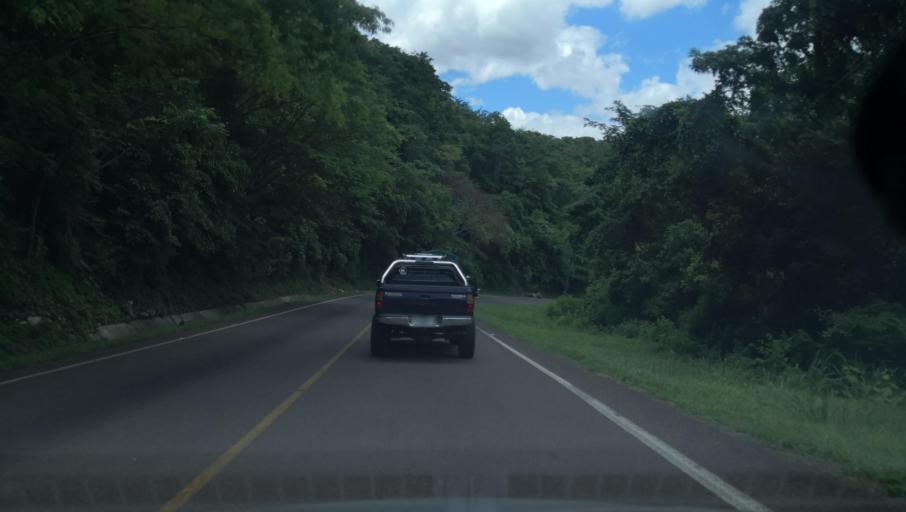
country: NI
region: Esteli
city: Condega
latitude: 13.2517
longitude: -86.3548
